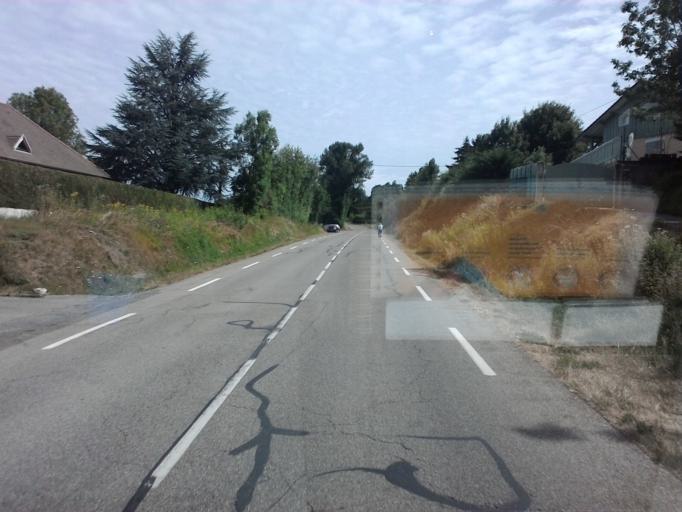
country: FR
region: Rhone-Alpes
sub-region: Departement de l'Isere
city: Bilieu
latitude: 45.4497
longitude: 5.5378
